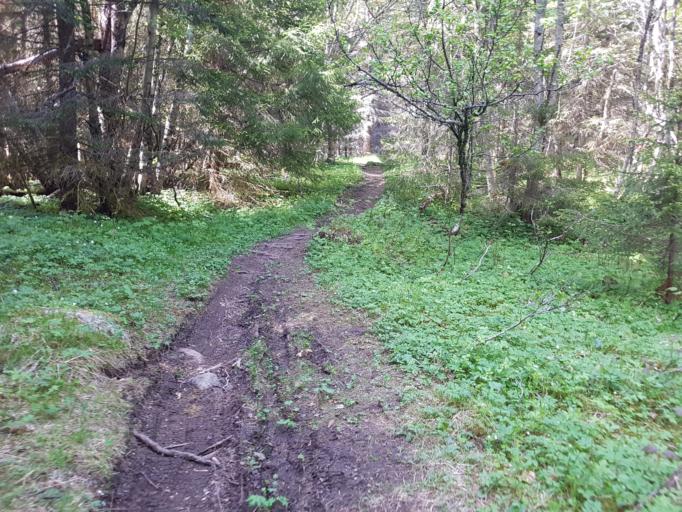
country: NO
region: Sor-Trondelag
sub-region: Trondheim
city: Trondheim
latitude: 63.4261
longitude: 10.3335
